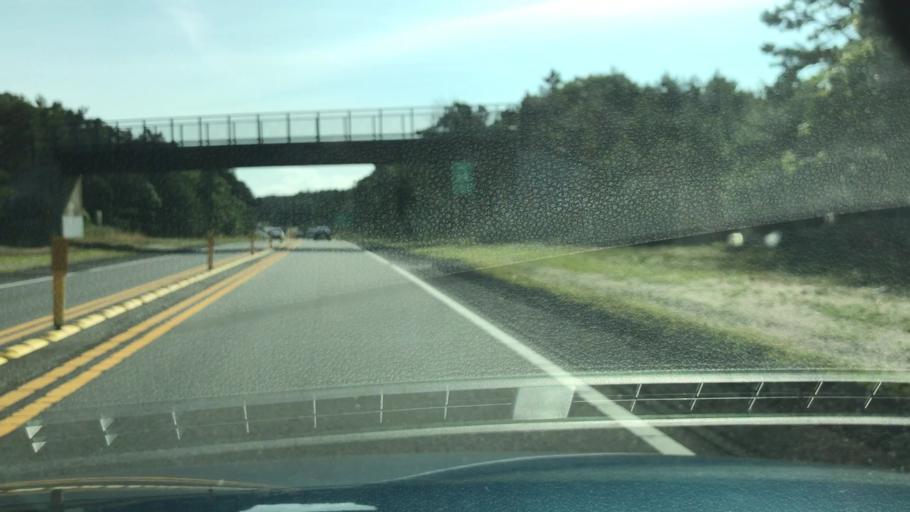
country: US
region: Massachusetts
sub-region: Barnstable County
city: Harwich Center
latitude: 41.7023
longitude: -70.0839
